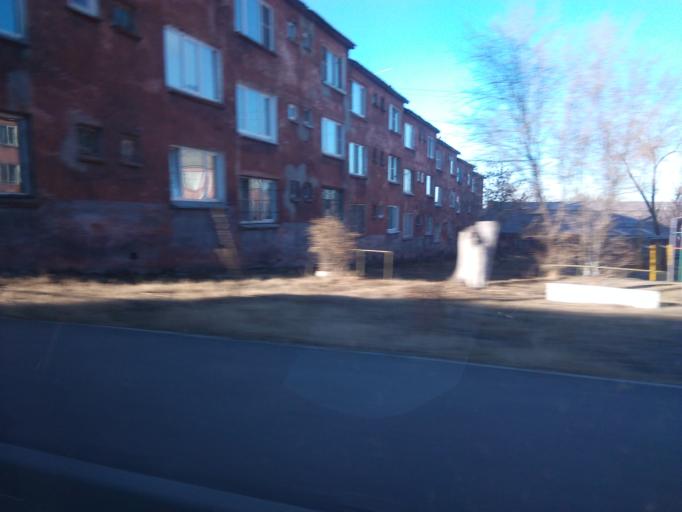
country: RU
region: Chelyabinsk
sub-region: Gorod Magnitogorsk
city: Magnitogorsk
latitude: 53.3885
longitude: 59.0572
